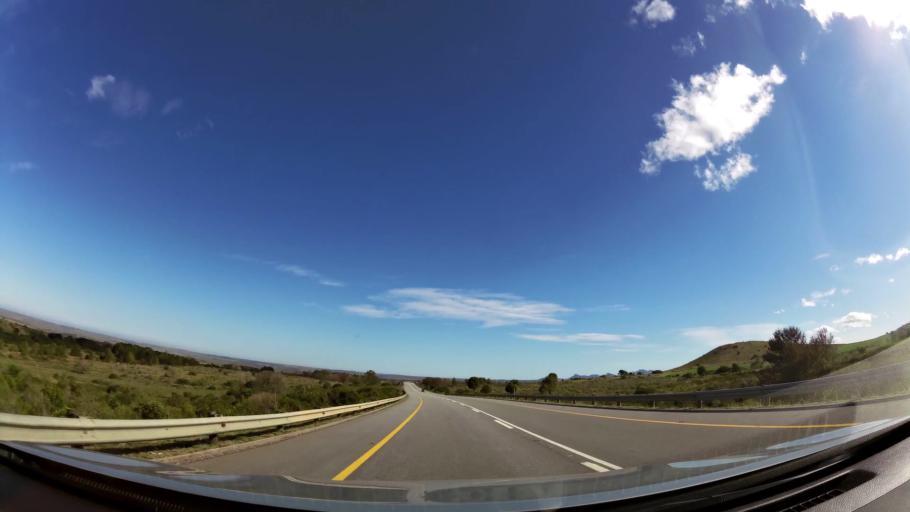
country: ZA
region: Eastern Cape
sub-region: Cacadu District Municipality
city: Kruisfontein
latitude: -33.9955
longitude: 24.6913
